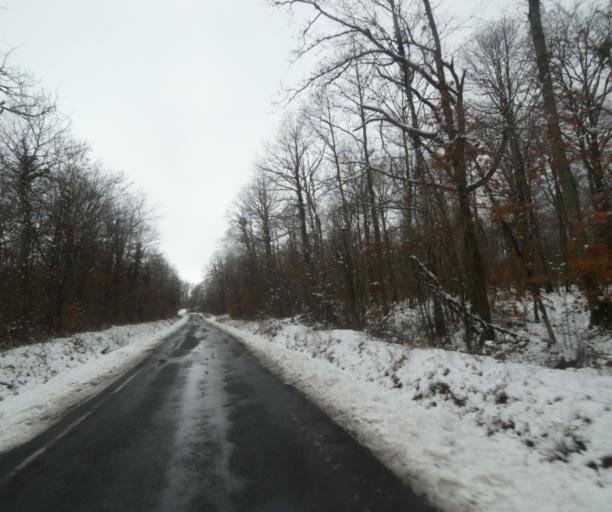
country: FR
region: Champagne-Ardenne
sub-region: Departement de la Haute-Marne
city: Laneuville-a-Remy
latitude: 48.4651
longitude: 4.8587
